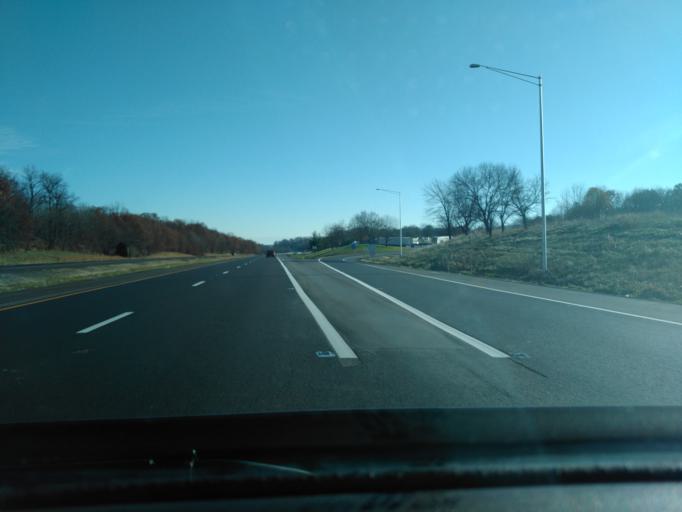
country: US
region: Illinois
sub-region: Madison County
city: Highland
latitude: 38.7858
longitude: -89.7066
